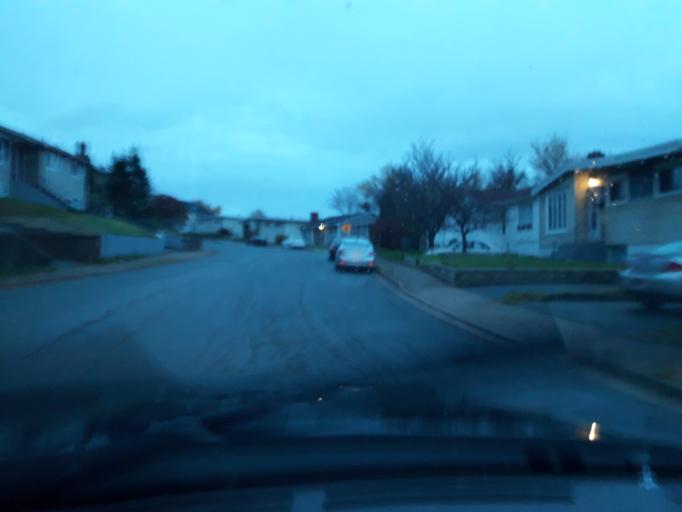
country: CA
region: Newfoundland and Labrador
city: St. John's
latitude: 47.5683
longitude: -52.7484
